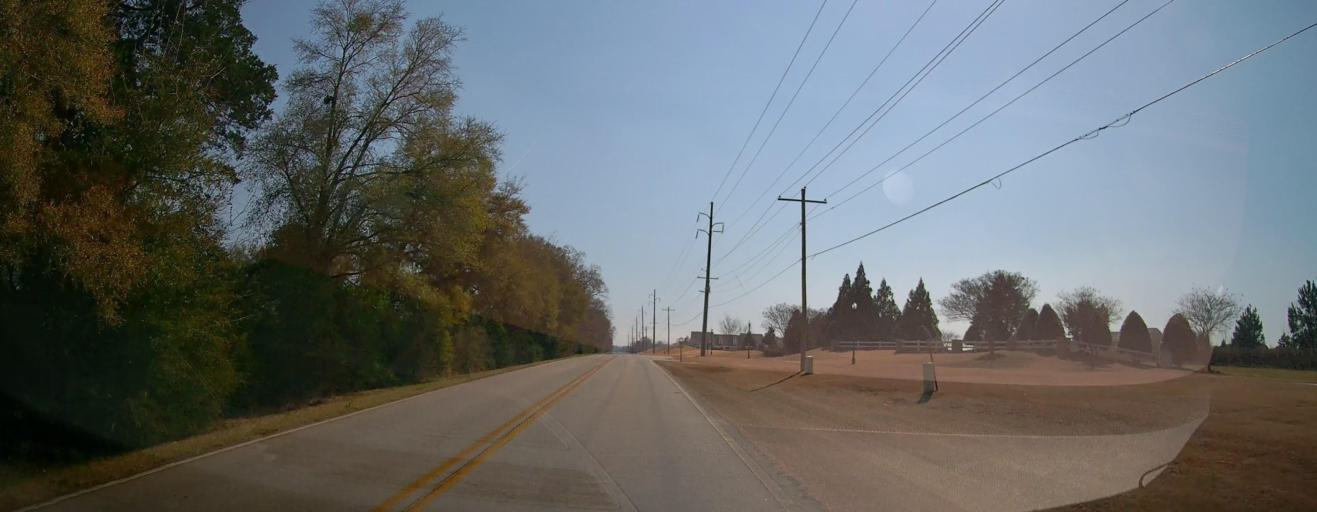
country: US
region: Georgia
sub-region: Houston County
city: Perry
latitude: 32.4781
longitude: -83.7590
